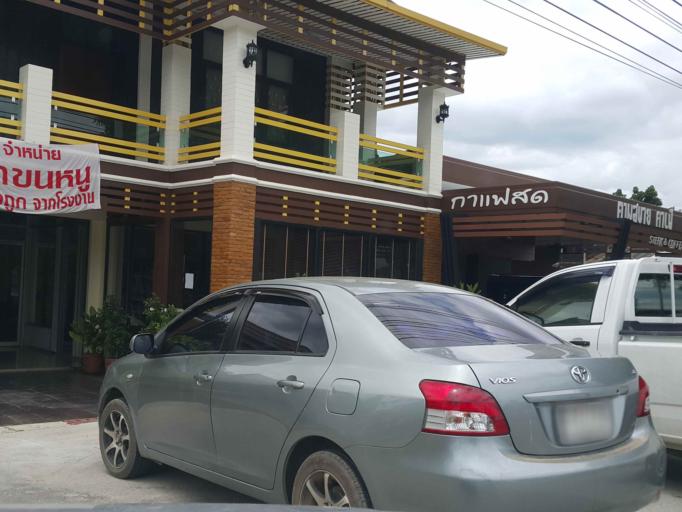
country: TH
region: Lamphun
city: Pa Sang
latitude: 18.4623
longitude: 98.9174
